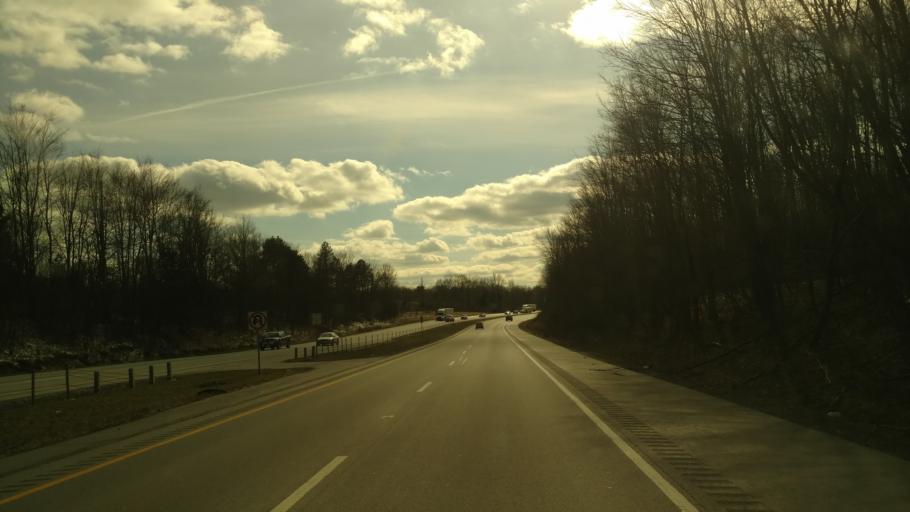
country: US
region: Ohio
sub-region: Medina County
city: Wadsworth
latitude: 41.0398
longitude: -81.7410
